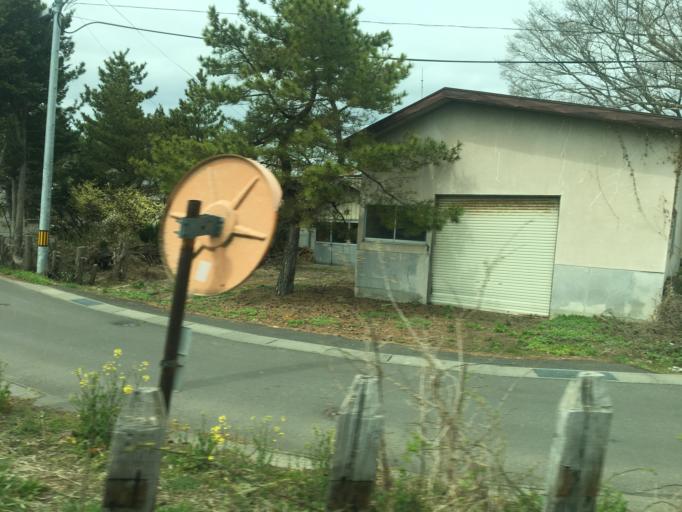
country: JP
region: Aomori
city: Shimokizukuri
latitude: 40.7965
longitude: 140.3784
